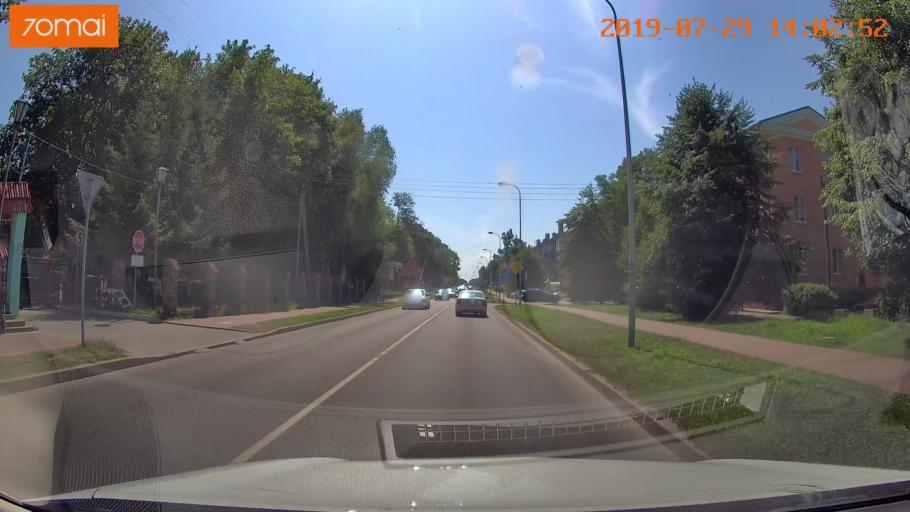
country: RU
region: Kaliningrad
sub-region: Gorod Kaliningrad
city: Baltiysk
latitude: 54.6609
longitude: 19.9149
